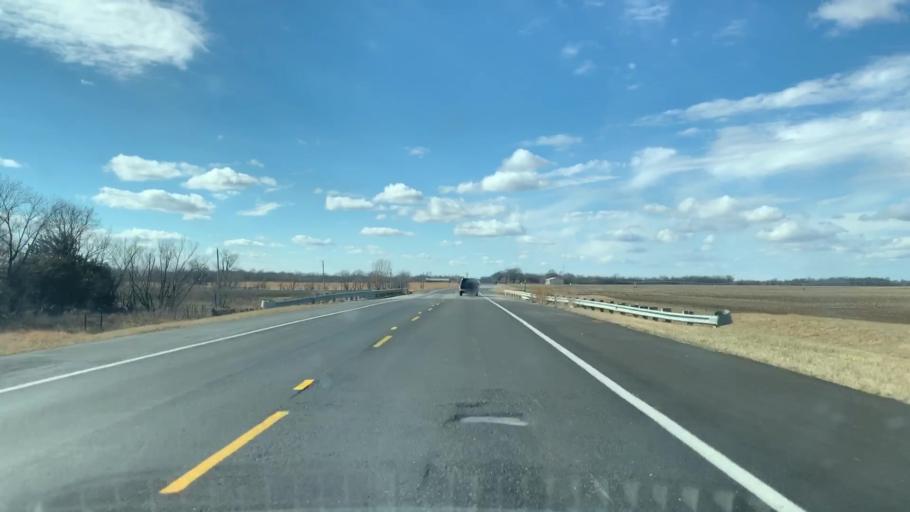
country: US
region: Kansas
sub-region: Labette County
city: Parsons
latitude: 37.3403
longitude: -95.1183
